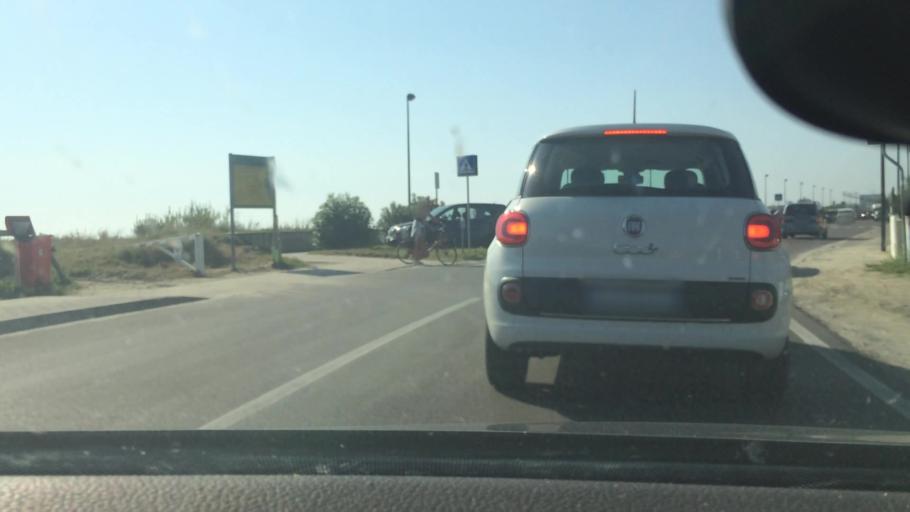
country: IT
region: Emilia-Romagna
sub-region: Provincia di Ferrara
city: Porto Garibaldi
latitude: 44.6878
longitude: 12.2399
